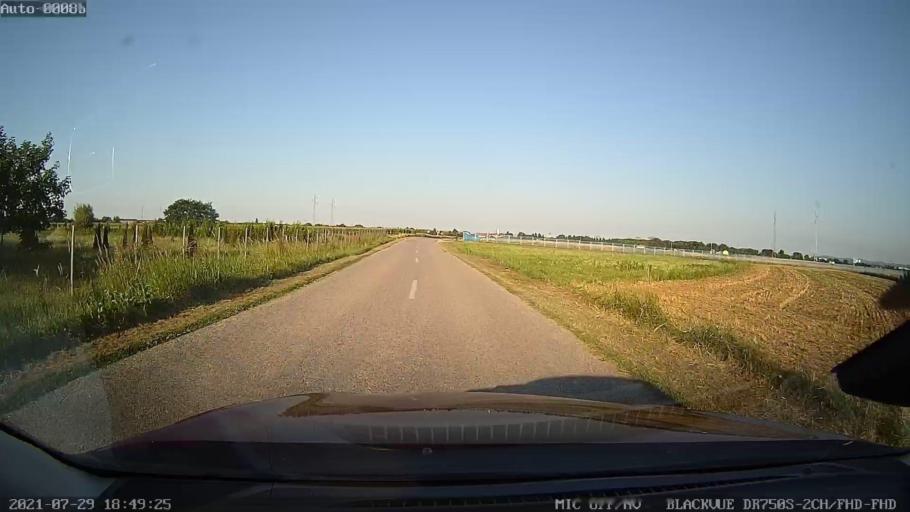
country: HR
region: Varazdinska
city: Nedeljanec
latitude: 46.3111
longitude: 16.3058
